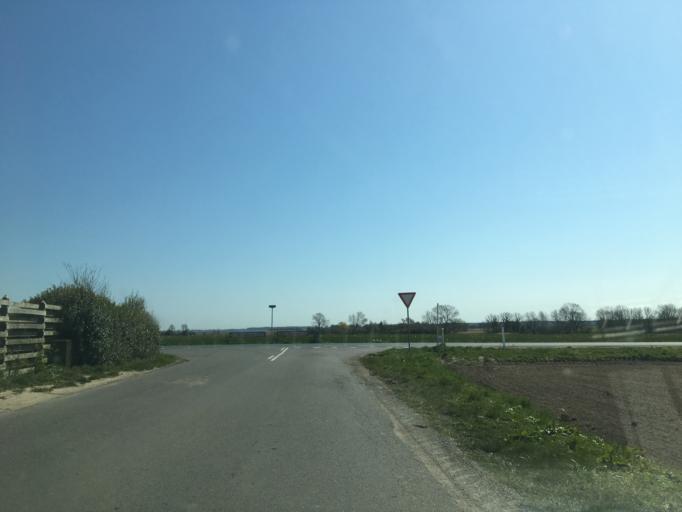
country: DK
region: Zealand
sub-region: Guldborgsund Kommune
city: Nykobing Falster
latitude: 54.7340
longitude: 11.8000
